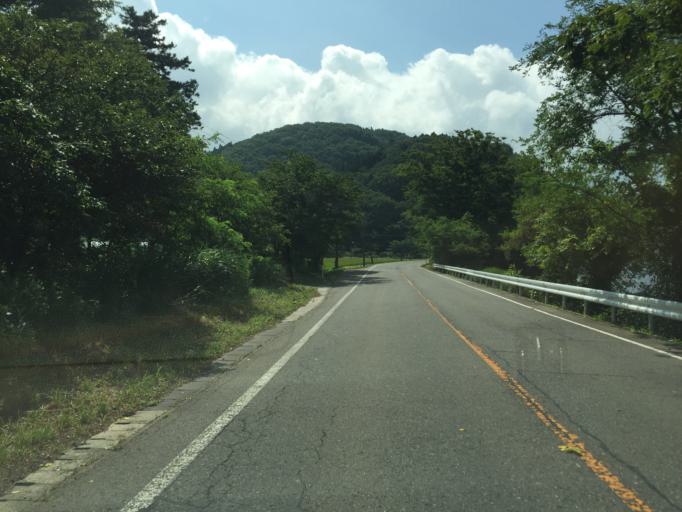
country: JP
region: Fukushima
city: Inawashiro
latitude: 37.4719
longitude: 140.1515
